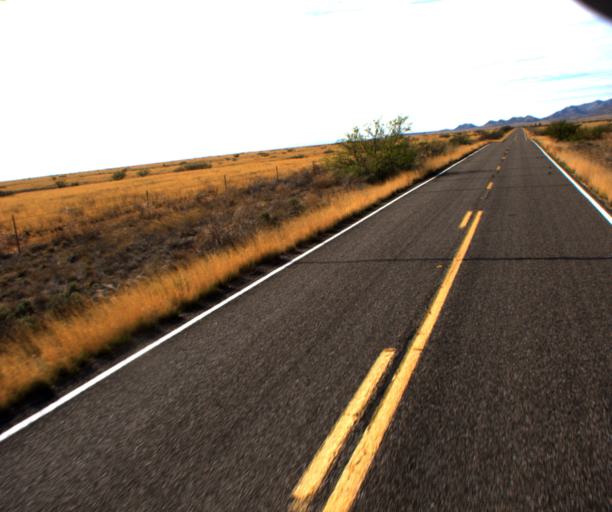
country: US
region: Arizona
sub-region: Cochise County
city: Willcox
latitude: 32.0829
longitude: -109.5236
